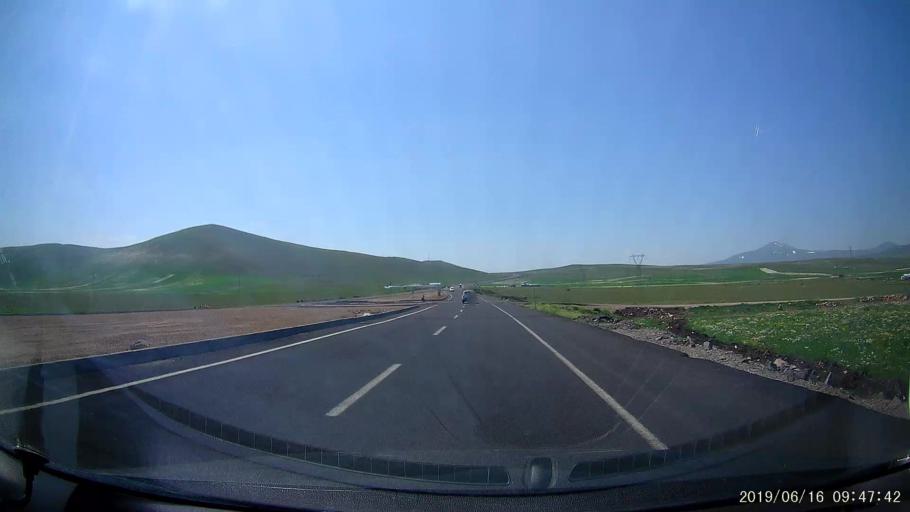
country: TR
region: Kars
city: Digor
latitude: 40.4427
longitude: 43.3470
